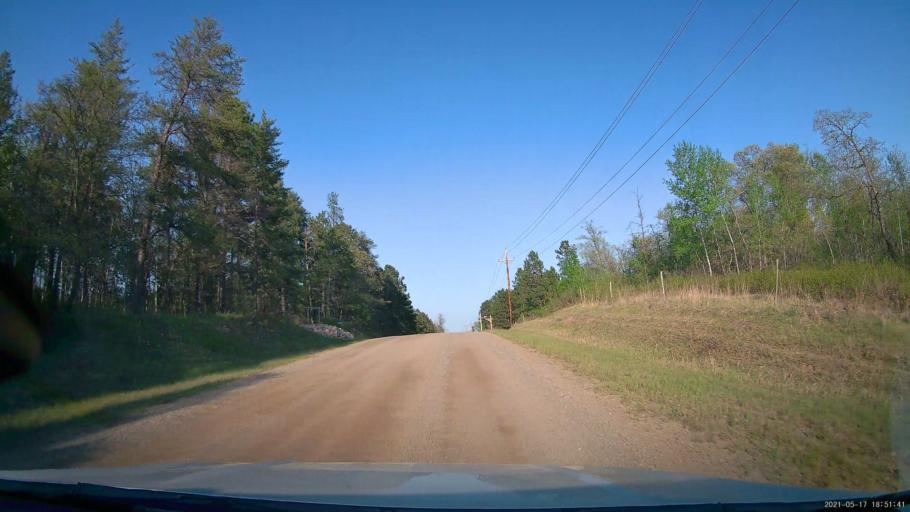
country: US
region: Minnesota
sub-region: Hubbard County
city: Park Rapids
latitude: 46.9438
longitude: -95.0092
